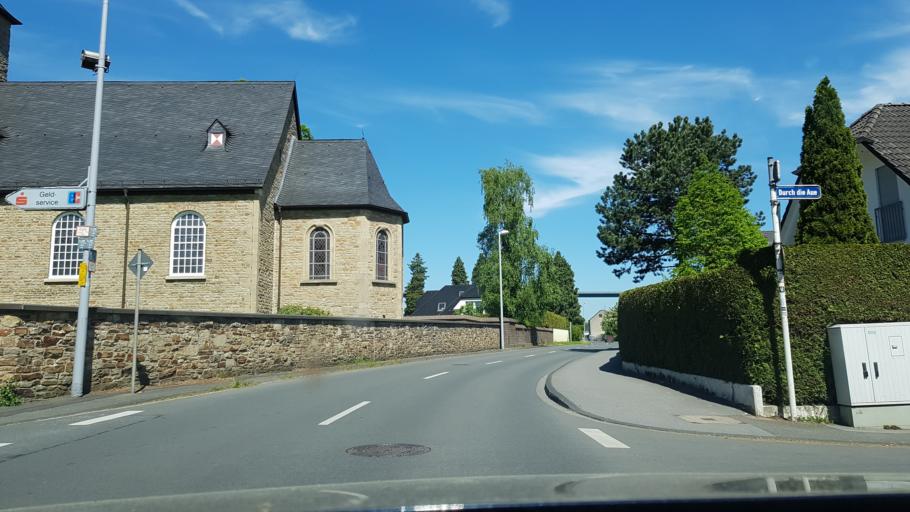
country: DE
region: North Rhine-Westphalia
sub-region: Regierungsbezirk Dusseldorf
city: Muelheim (Ruhr)
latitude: 51.3720
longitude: 6.9044
